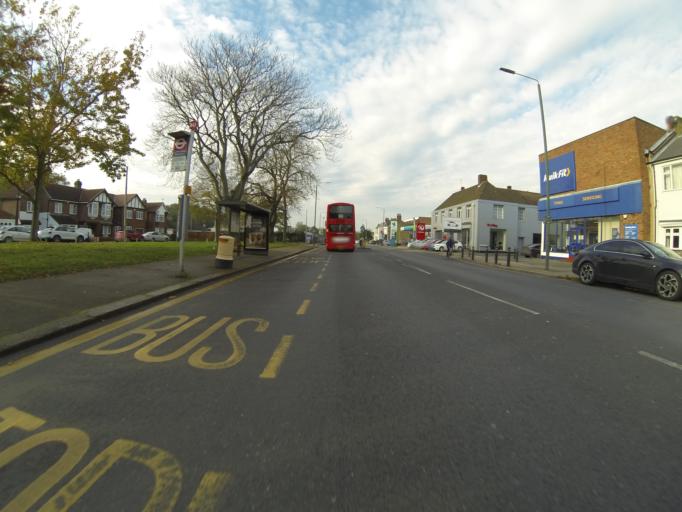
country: GB
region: England
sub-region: Greater London
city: Welling
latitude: 51.4604
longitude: 0.1205
